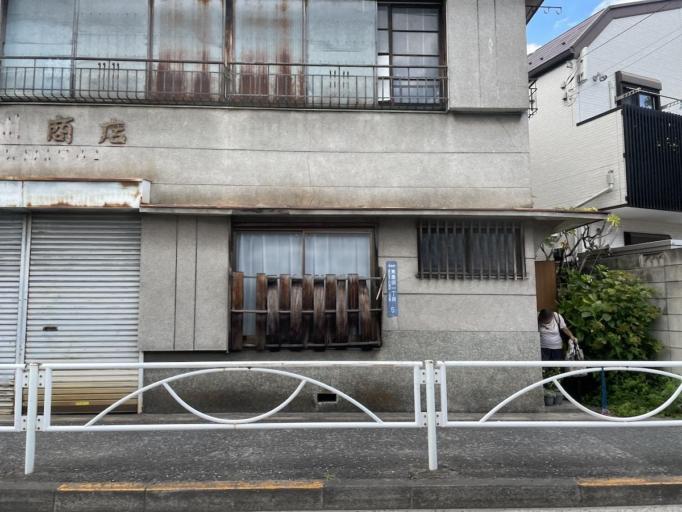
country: JP
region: Tokyo
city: Urayasu
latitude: 35.7154
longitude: 139.8303
